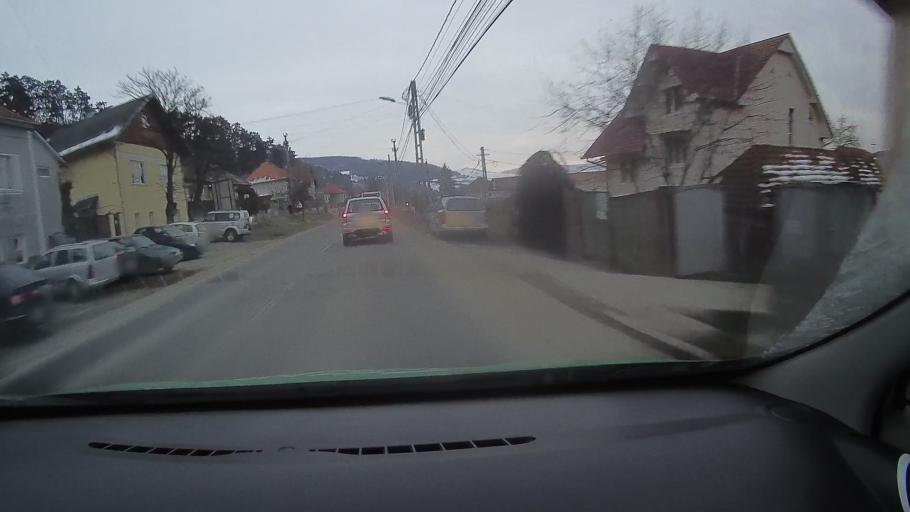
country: RO
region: Harghita
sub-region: Municipiul Odorheiu Secuiesc
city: Odorheiu Secuiesc
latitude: 46.2943
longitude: 25.2895
